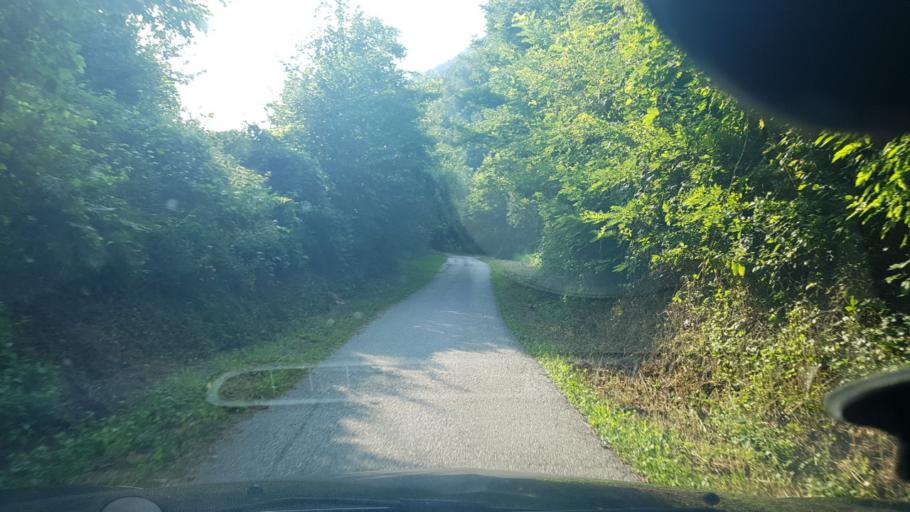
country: HR
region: Krapinsko-Zagorska
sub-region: Grad Krapina
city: Krapina
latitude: 46.1784
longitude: 15.8831
